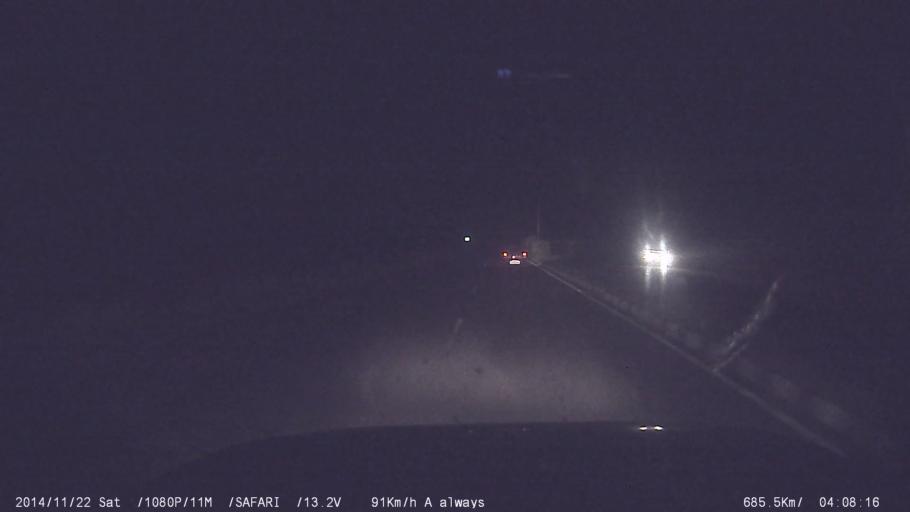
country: IN
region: Tamil Nadu
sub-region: Erode
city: Perundurai
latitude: 11.2816
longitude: 77.5579
